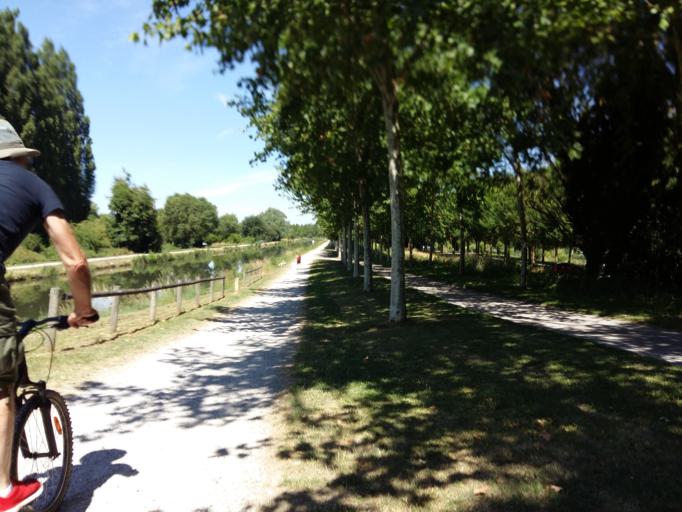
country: FR
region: Picardie
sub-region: Departement de la Somme
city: Amiens
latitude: 49.9096
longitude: 2.2810
